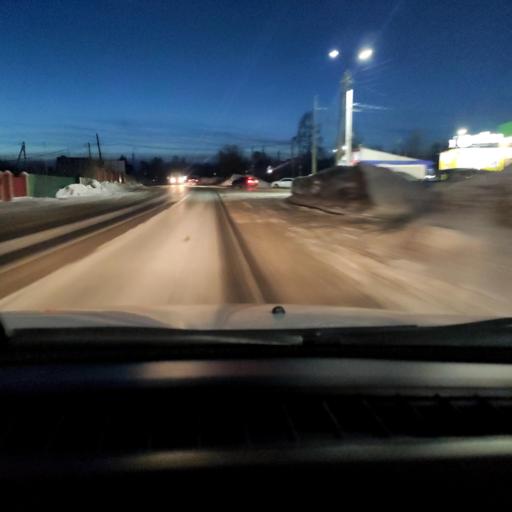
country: RU
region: Samara
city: Kinel'
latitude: 53.2693
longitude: 50.5814
